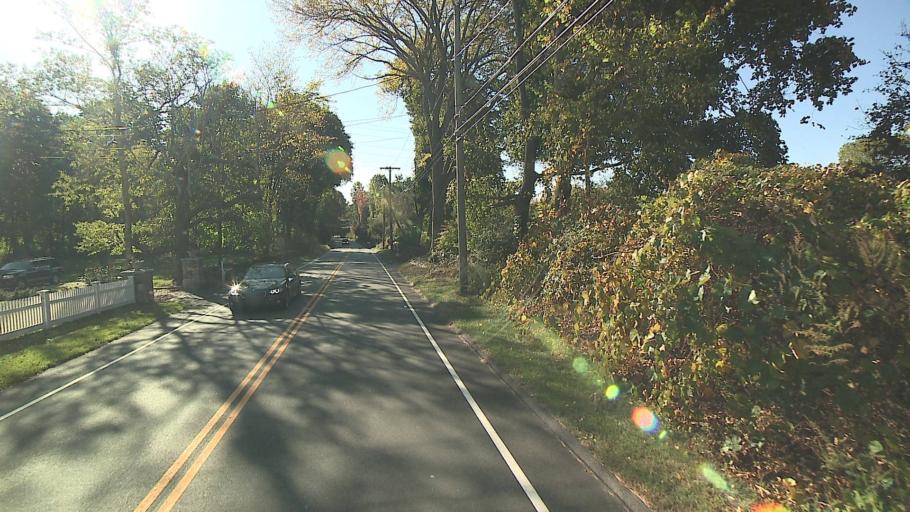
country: US
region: Connecticut
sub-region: Fairfield County
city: Wilton
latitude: 41.1820
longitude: -73.3938
